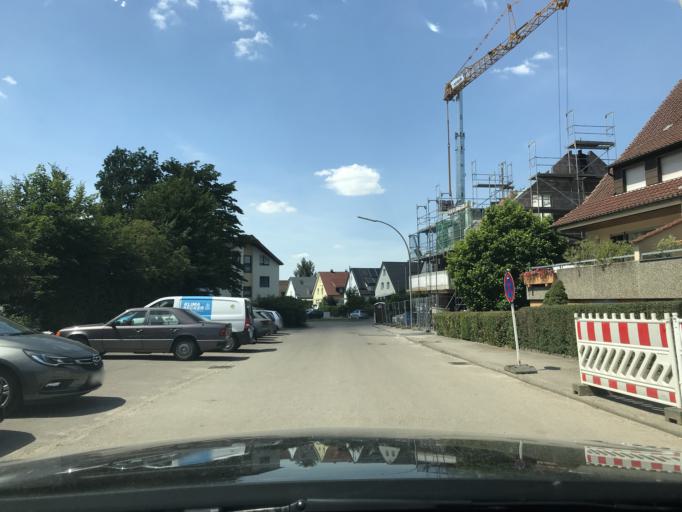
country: DE
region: Baden-Wuerttemberg
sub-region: Regierungsbezirk Stuttgart
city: Weinstadt-Endersbach
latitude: 48.8085
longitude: 9.3710
